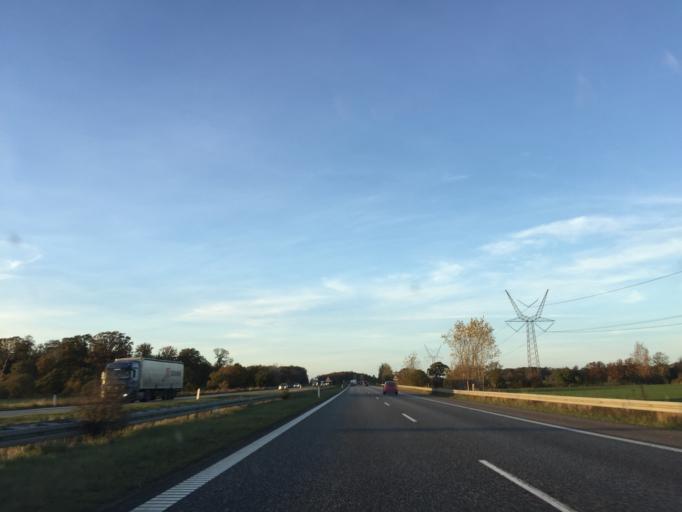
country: DK
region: South Denmark
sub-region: Kolding Kommune
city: Kolding
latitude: 55.4509
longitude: 9.4513
